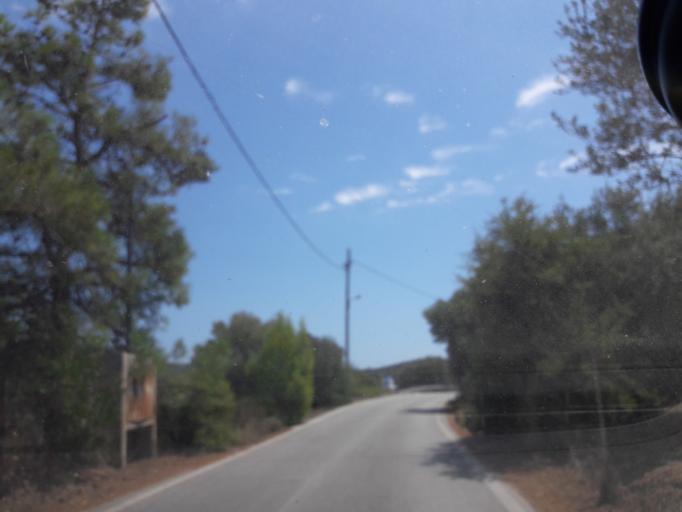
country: GR
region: Central Macedonia
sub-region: Nomos Chalkidikis
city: Nea Roda
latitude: 40.3222
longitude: 23.9215
